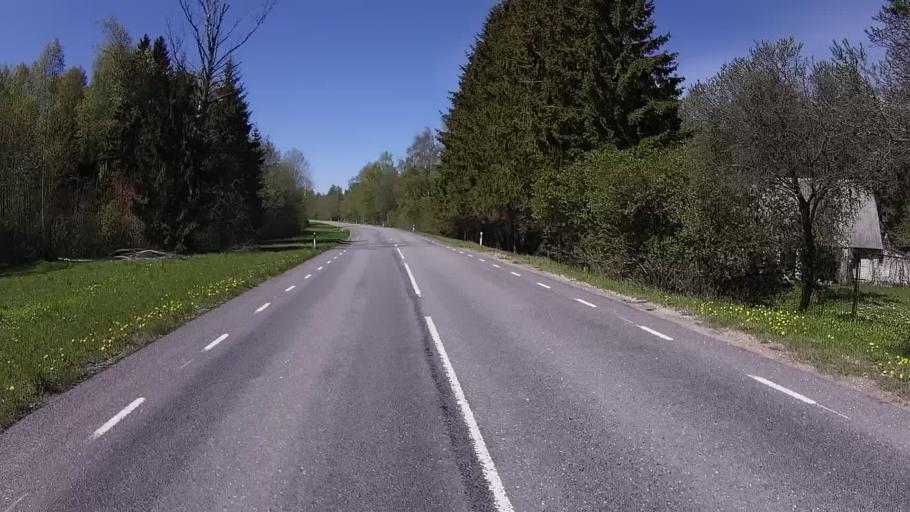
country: EE
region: Raplamaa
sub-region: Kehtna vald
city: Kehtna
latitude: 59.0529
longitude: 25.0182
